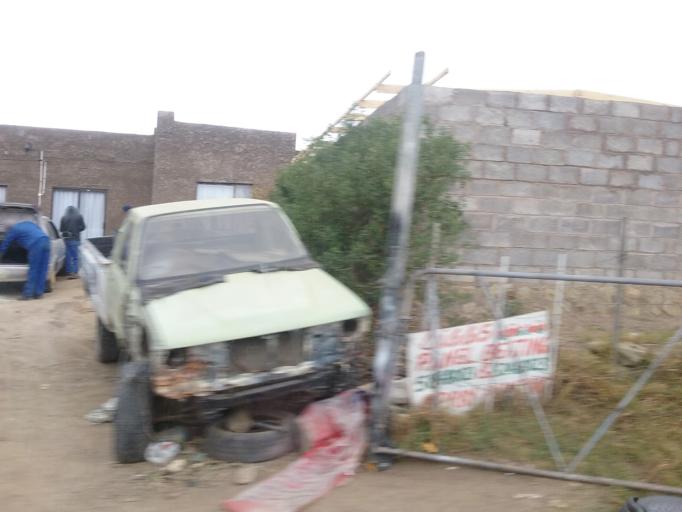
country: LS
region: Maseru
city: Maseru
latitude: -29.3263
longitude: 27.5077
